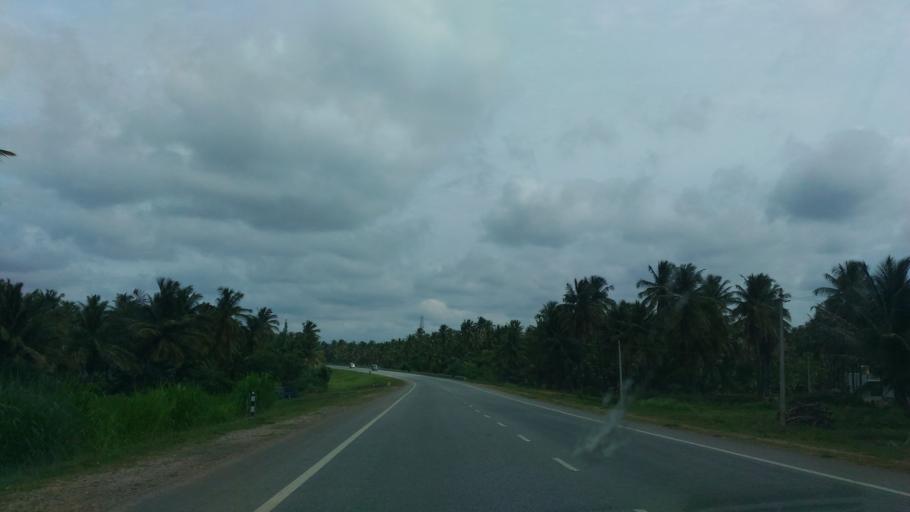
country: IN
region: Karnataka
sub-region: Hassan
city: Channarayapatna
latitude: 12.9289
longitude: 76.4067
